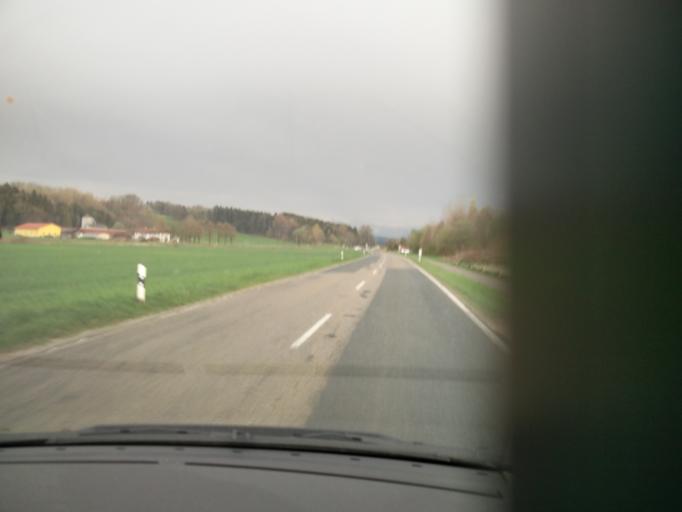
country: DE
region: Bavaria
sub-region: Upper Bavaria
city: Halfing
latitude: 47.9446
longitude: 12.2788
